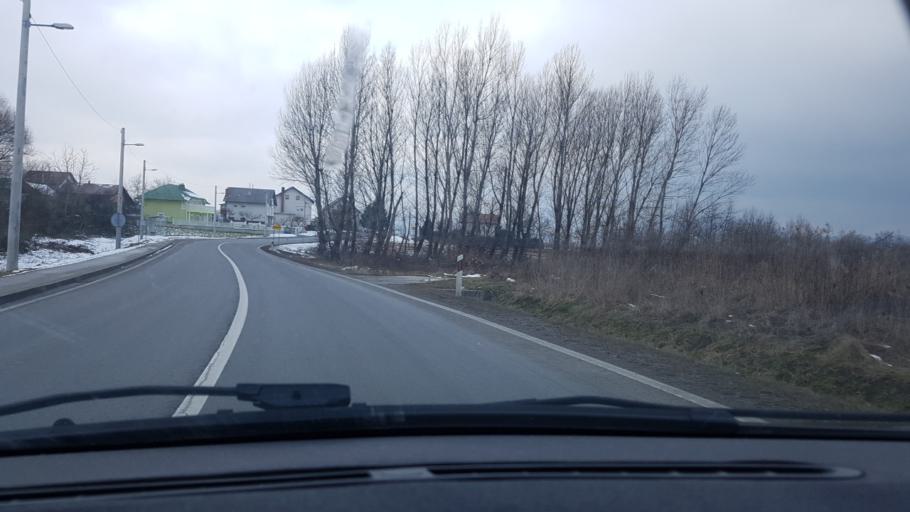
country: HR
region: Varazdinska
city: Ivanec
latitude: 46.2231
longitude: 16.0949
